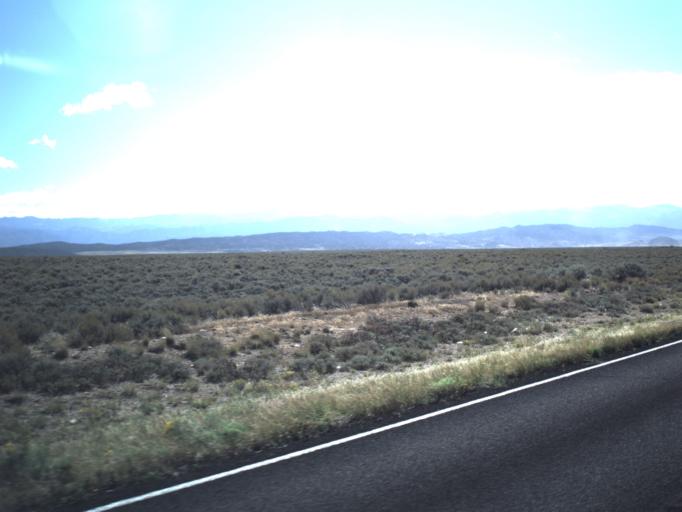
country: US
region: Utah
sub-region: Iron County
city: Enoch
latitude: 37.9990
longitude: -112.9987
